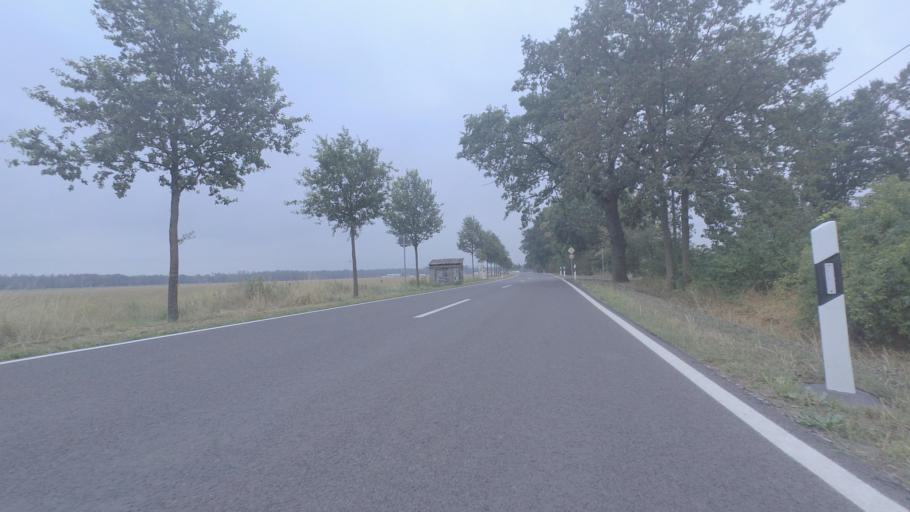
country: DE
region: Brandenburg
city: Paulinenaue
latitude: 52.6596
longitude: 12.7415
